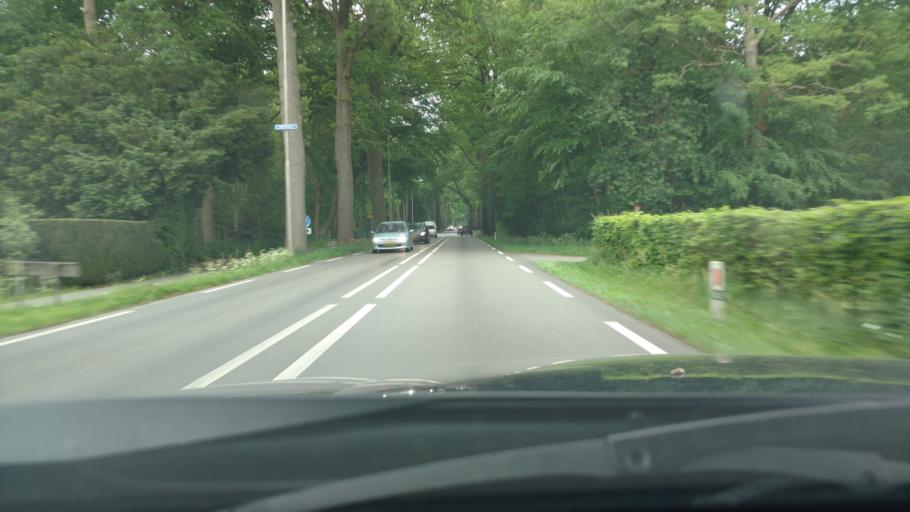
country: NL
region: Gelderland
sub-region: Gemeente Lochem
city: Gorssel
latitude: 52.1923
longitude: 6.2038
